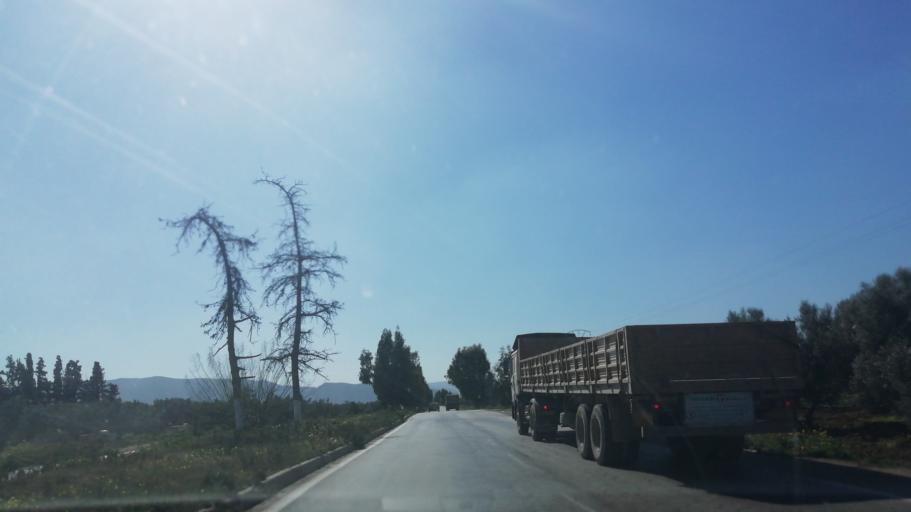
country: DZ
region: Mascara
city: Sig
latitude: 35.5595
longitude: -0.2074
